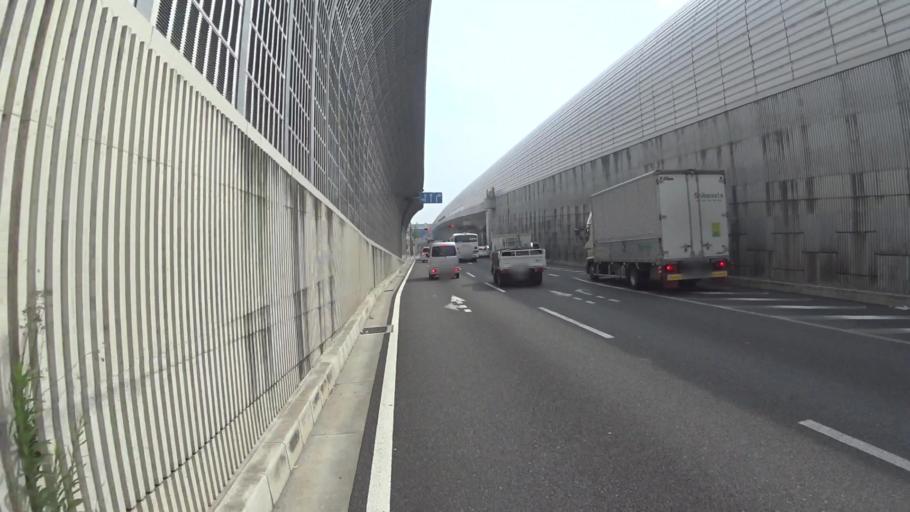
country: JP
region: Kyoto
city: Yawata
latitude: 34.8341
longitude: 135.7229
